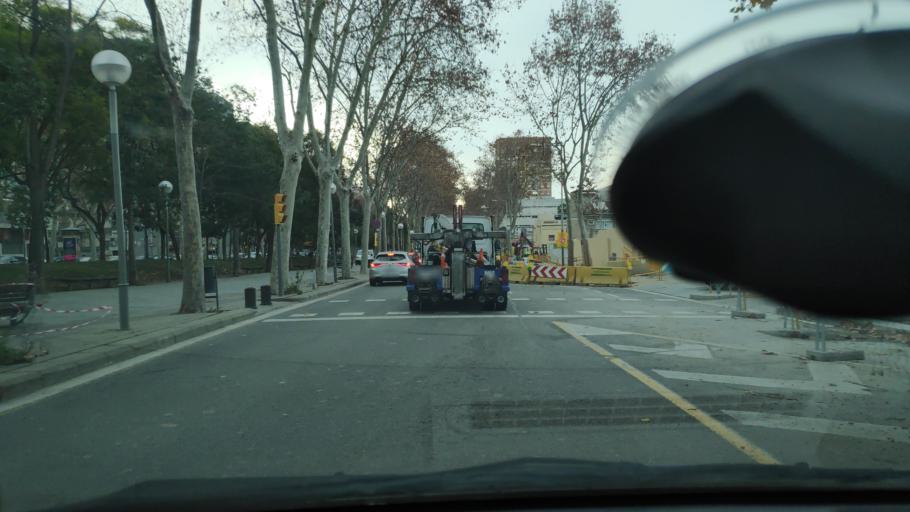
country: ES
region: Catalonia
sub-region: Provincia de Barcelona
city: Sant Marti
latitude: 41.4182
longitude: 2.2097
